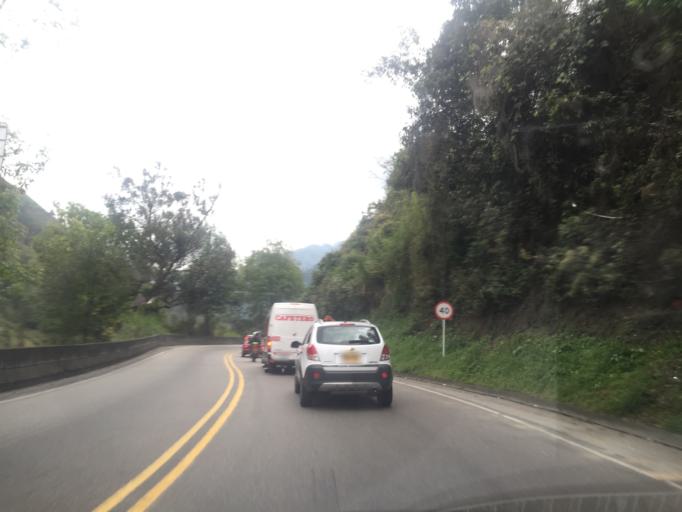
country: CO
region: Tolima
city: Cajamarca
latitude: 4.4347
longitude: -75.4633
